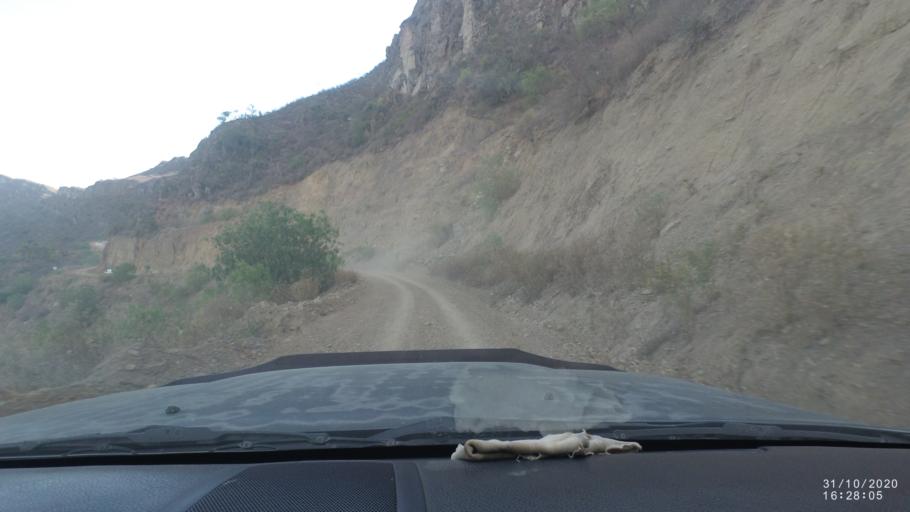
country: BO
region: Chuquisaca
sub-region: Provincia Zudanez
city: Mojocoya
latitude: -18.4103
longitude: -64.5864
